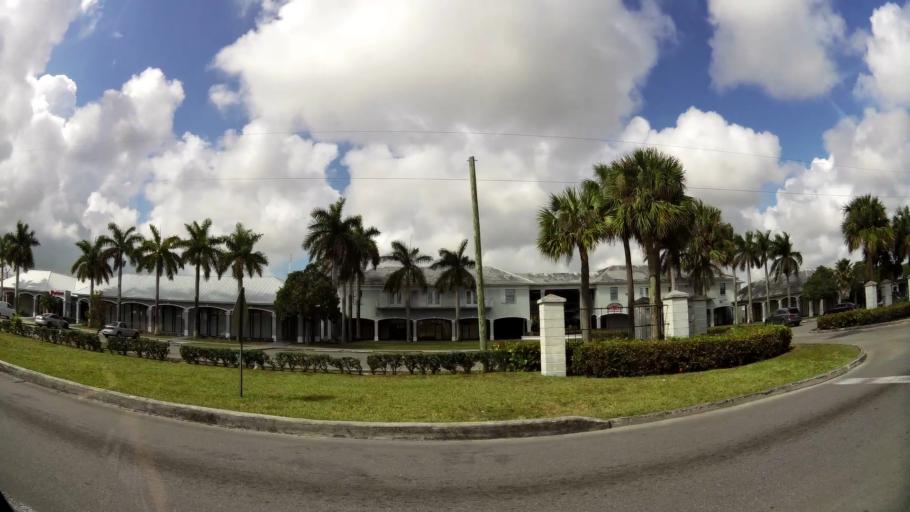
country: BS
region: Freeport
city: Freeport
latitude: 26.5341
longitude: -78.6955
